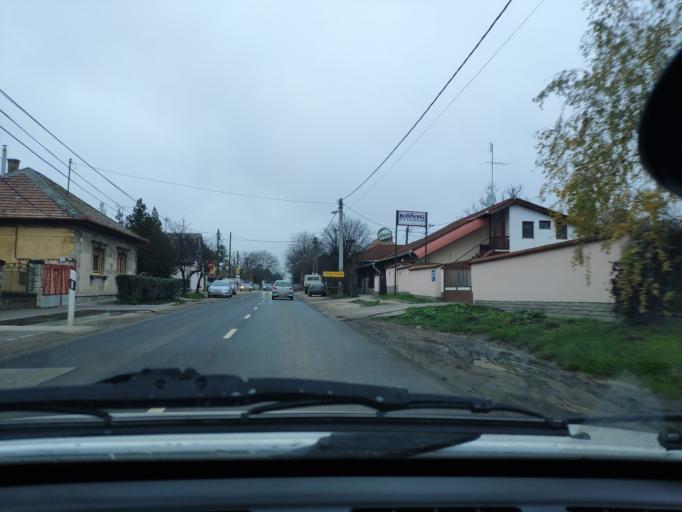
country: HU
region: Pest
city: Soskut
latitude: 47.4035
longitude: 18.8348
